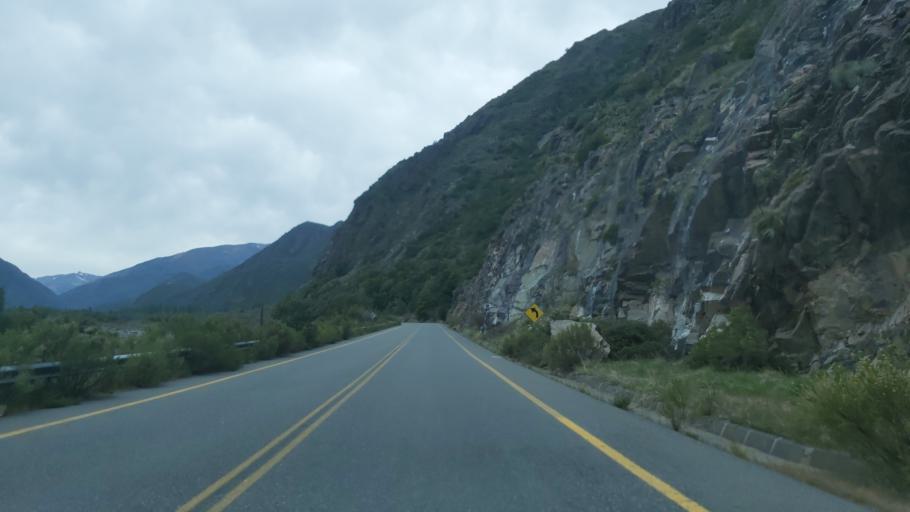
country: CL
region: Maule
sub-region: Provincia de Linares
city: Colbun
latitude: -35.8040
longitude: -70.8914
